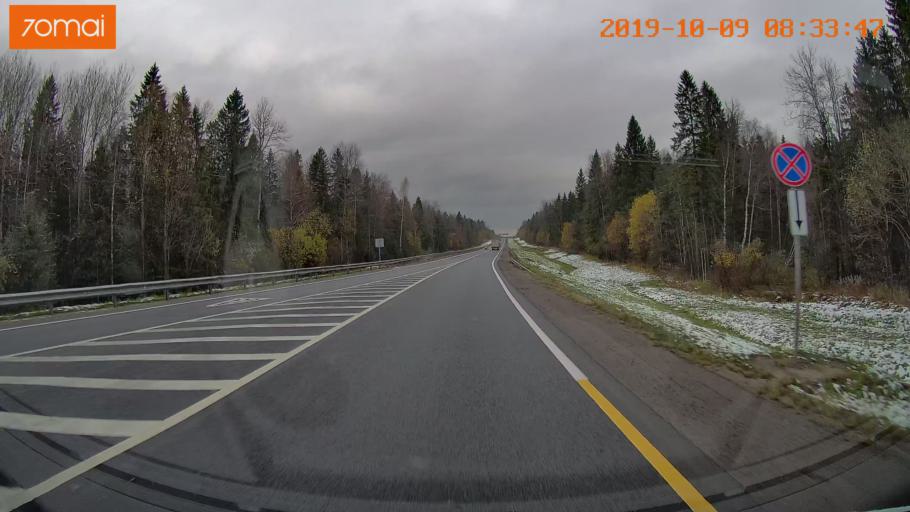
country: RU
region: Vologda
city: Gryazovets
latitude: 58.8873
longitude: 40.1901
